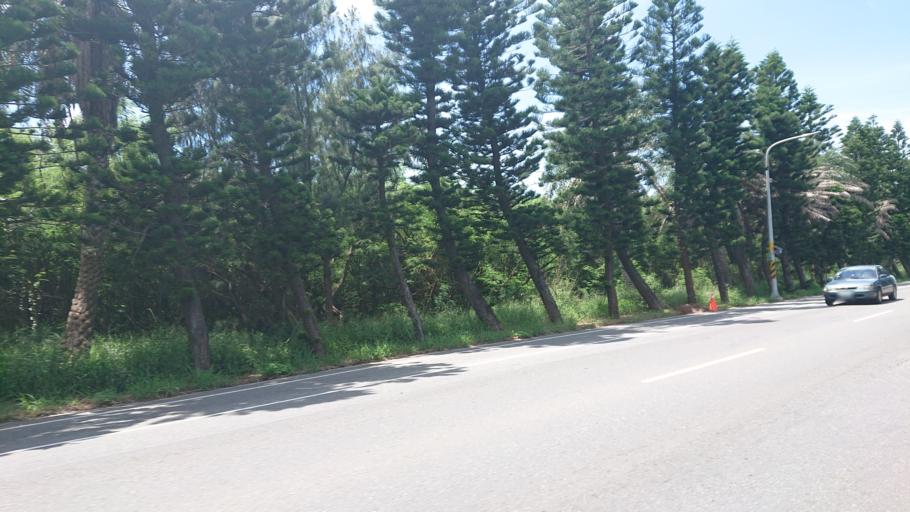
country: TW
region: Taiwan
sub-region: Penghu
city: Ma-kung
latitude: 23.5958
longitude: 119.6132
